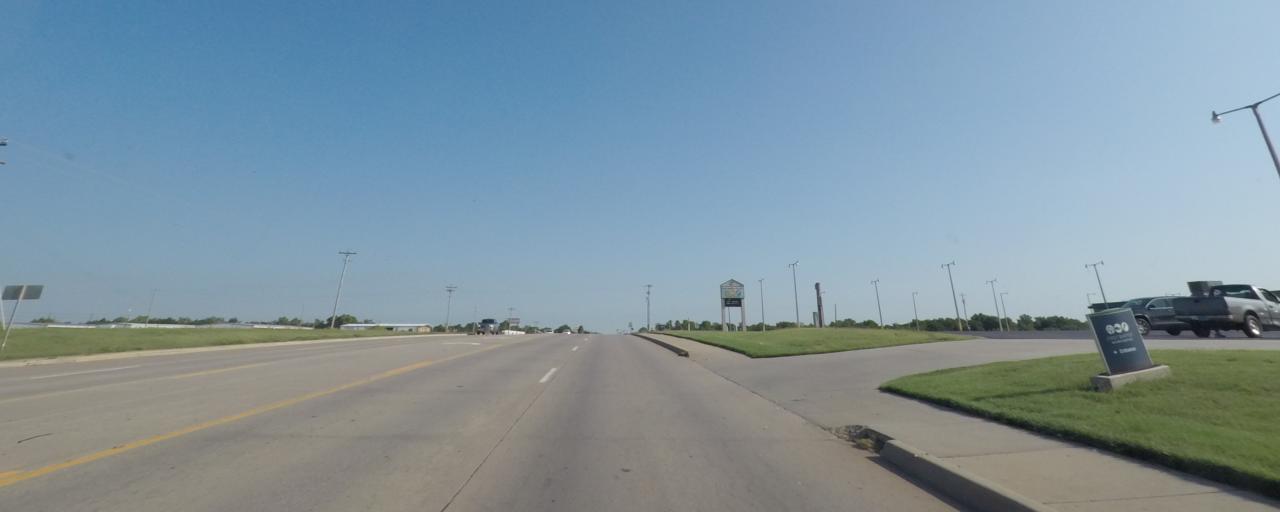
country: US
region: Oklahoma
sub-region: McClain County
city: Newcastle
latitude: 35.2624
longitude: -97.6001
